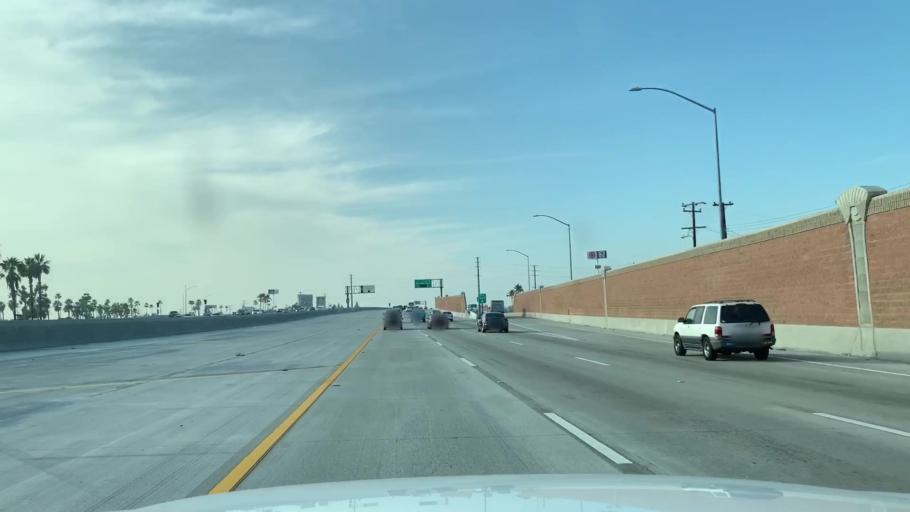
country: US
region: California
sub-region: Los Angeles County
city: Norwalk
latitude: 33.9001
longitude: -118.0577
